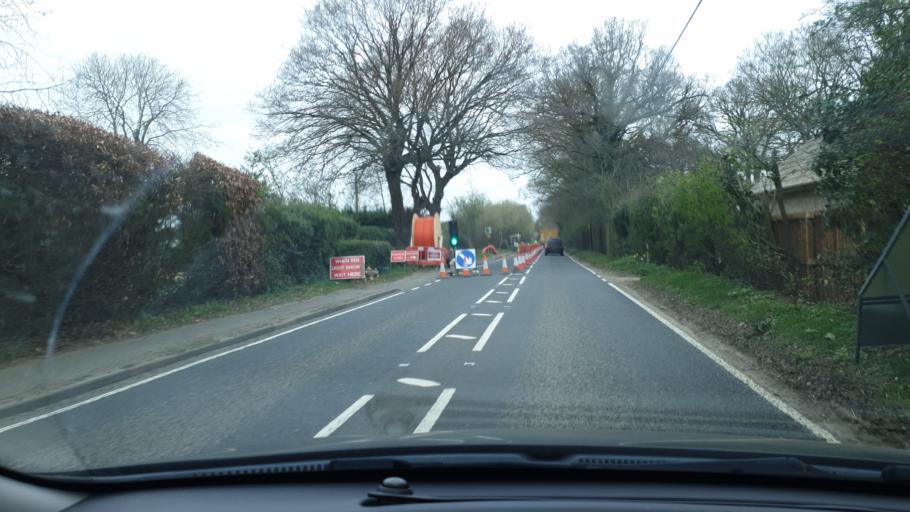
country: GB
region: England
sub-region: Essex
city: Great Horkesley
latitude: 51.9430
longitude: 0.8756
